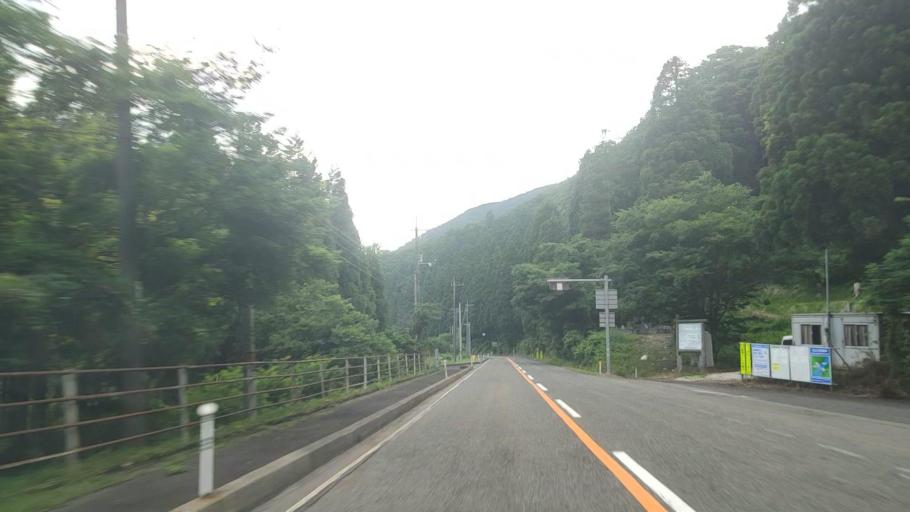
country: JP
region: Tottori
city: Kurayoshi
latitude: 35.3178
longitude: 133.8967
